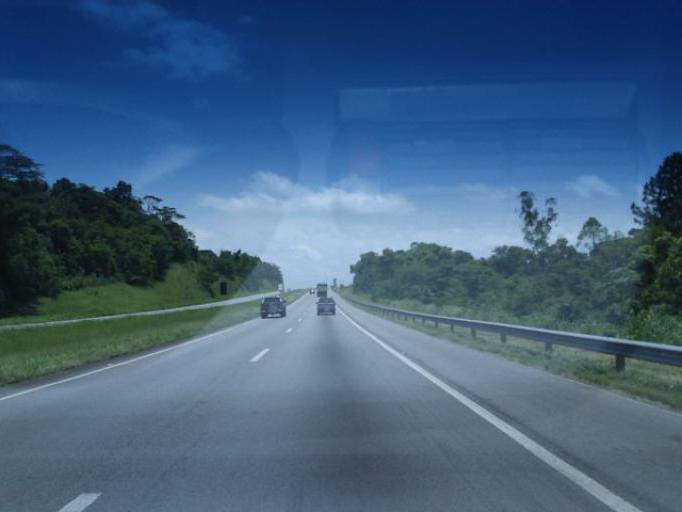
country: BR
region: Sao Paulo
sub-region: Registro
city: Registro
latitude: -24.4494
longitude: -47.8073
